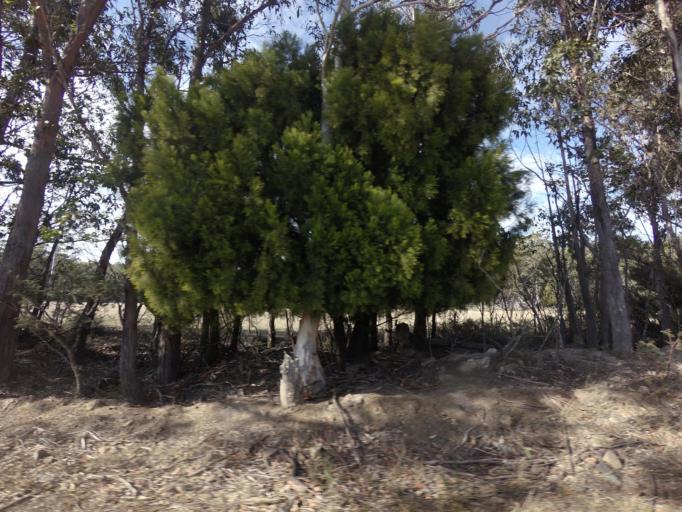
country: AU
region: Tasmania
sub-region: Sorell
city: Sorell
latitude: -42.5088
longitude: 147.4774
